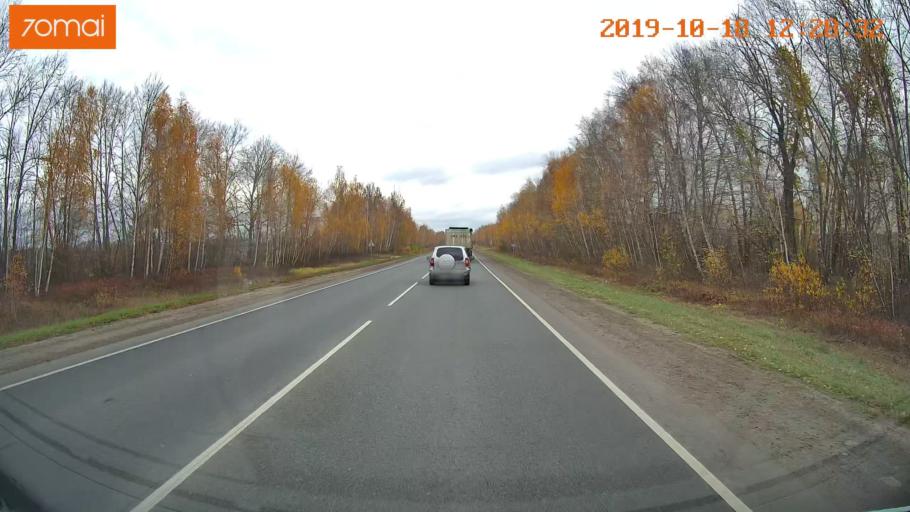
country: RU
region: Rjazan
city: Ryazan'
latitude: 54.5726
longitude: 39.5701
